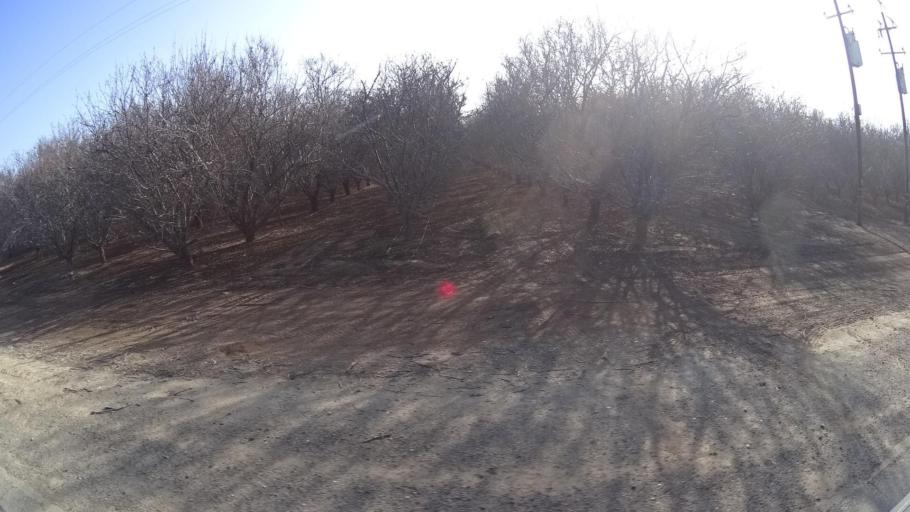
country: US
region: California
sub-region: Kern County
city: Maricopa
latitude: 35.1012
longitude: -119.3217
